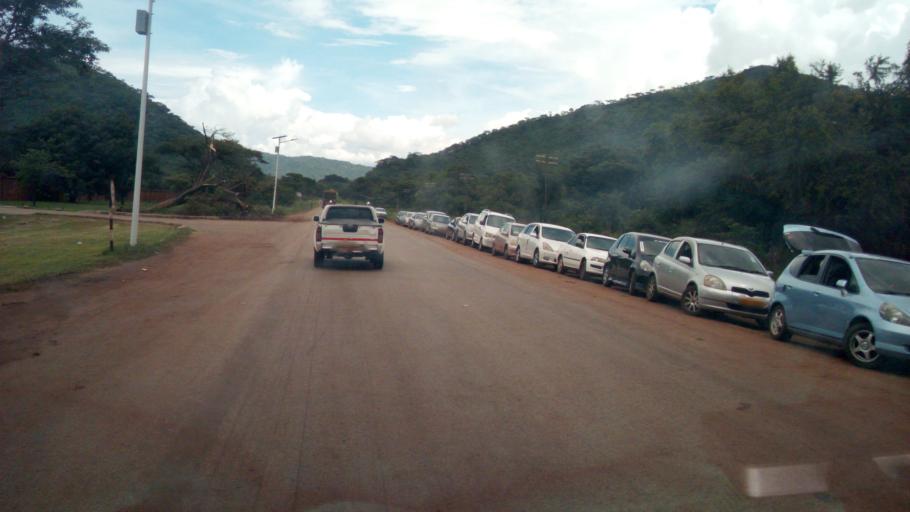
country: ZW
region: Mashonaland Central
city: Mazowe
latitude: -17.5112
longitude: 30.9778
